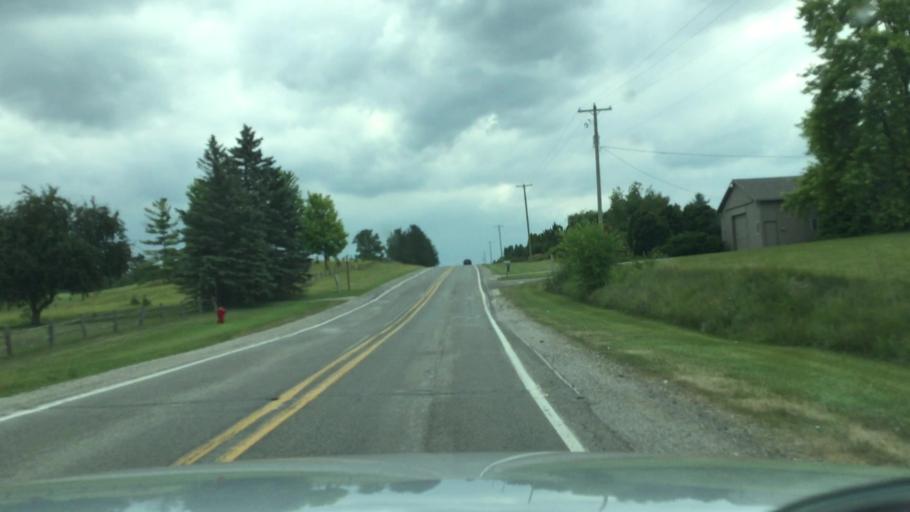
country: US
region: Michigan
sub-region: Saginaw County
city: Frankenmuth
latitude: 43.3272
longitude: -83.7581
